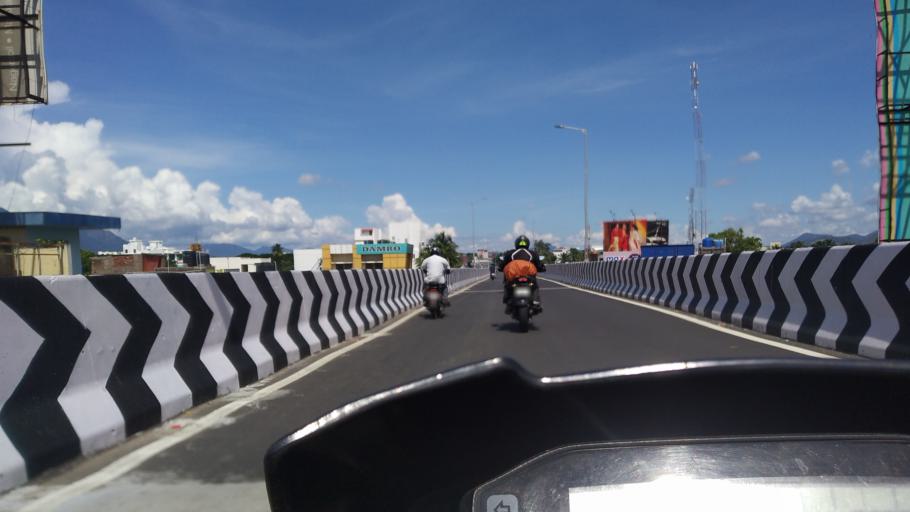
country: IN
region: Tamil Nadu
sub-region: Salem
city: Salem
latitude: 11.6766
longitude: 78.1392
